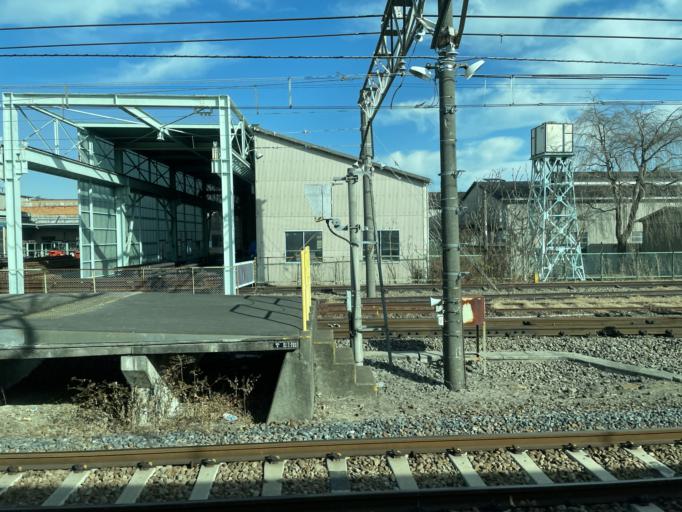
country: JP
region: Saitama
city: Fukayacho
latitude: 36.2049
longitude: 139.2396
